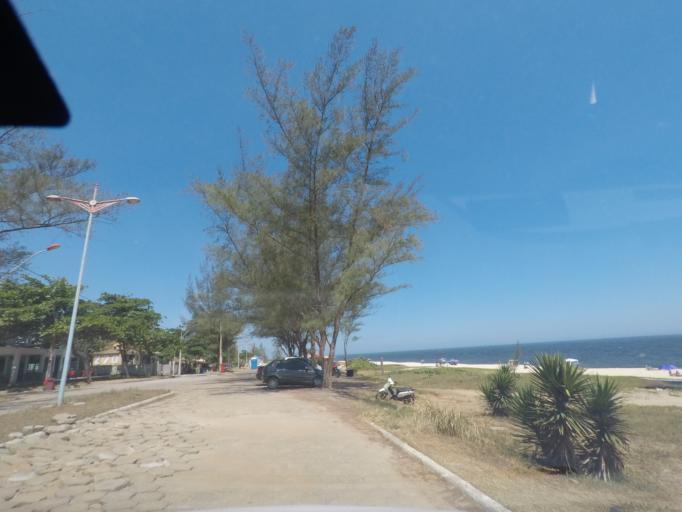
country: BR
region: Rio de Janeiro
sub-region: Marica
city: Marica
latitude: -22.9738
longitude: -42.9282
